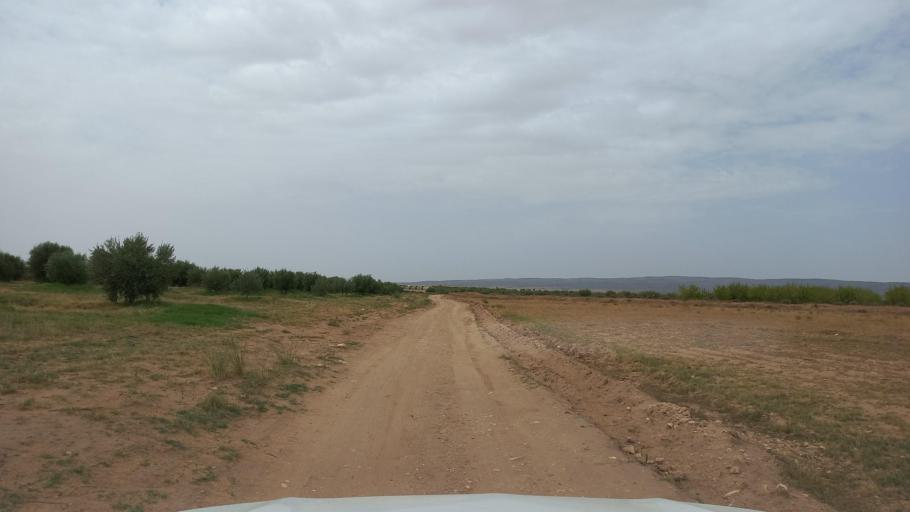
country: TN
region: Al Qasrayn
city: Kasserine
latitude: 35.2867
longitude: 9.0229
